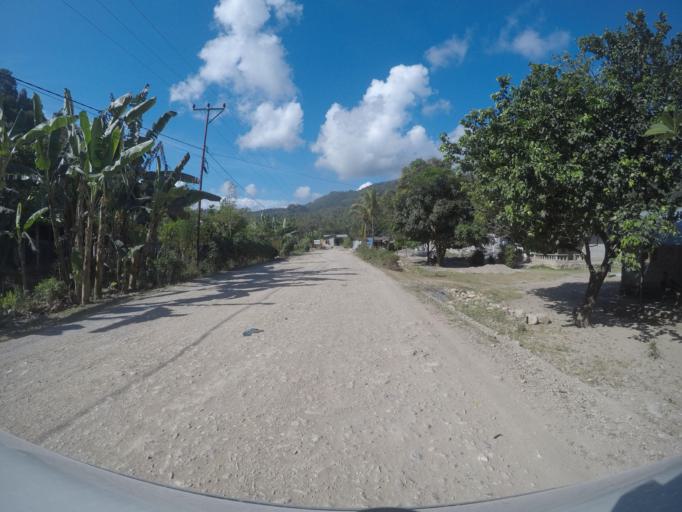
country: TL
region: Viqueque
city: Viqueque
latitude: -8.7959
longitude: 126.5569
